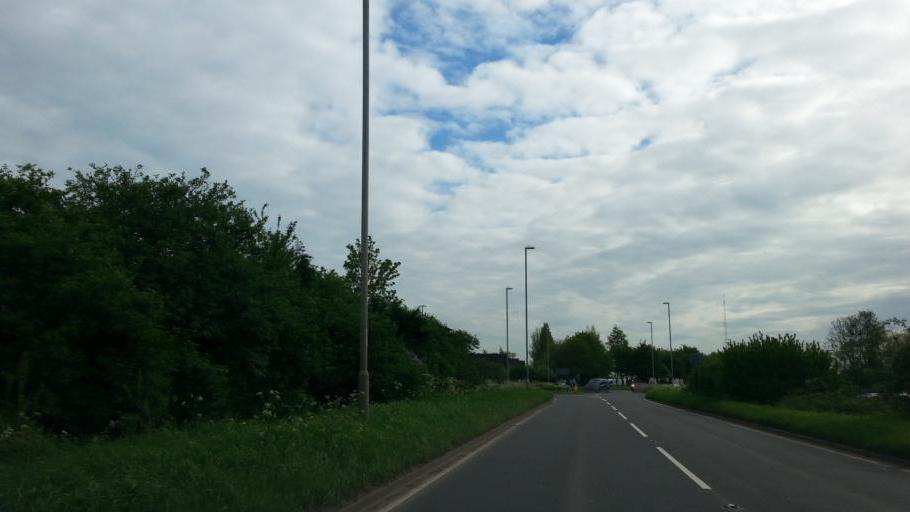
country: GB
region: England
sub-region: Cambridgeshire
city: Chatteris
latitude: 52.4530
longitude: 0.0395
